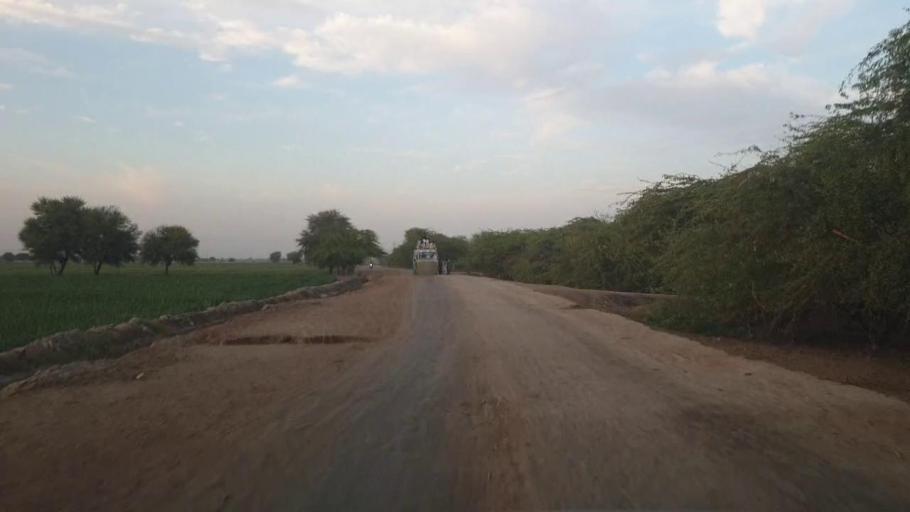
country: PK
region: Sindh
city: Umarkot
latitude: 25.2641
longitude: 69.6762
